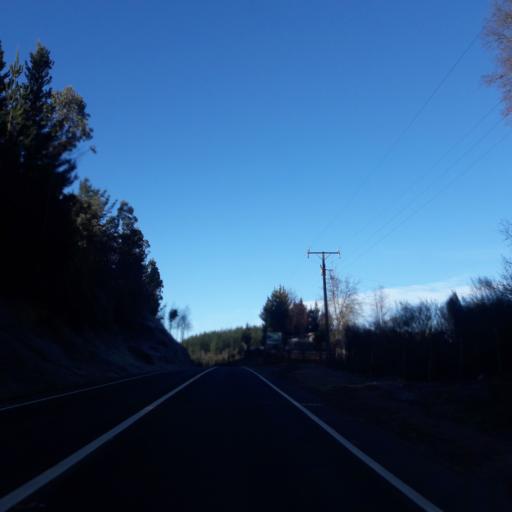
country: CL
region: Biobio
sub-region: Provincia de Biobio
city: La Laja
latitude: -37.2786
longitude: -72.9474
